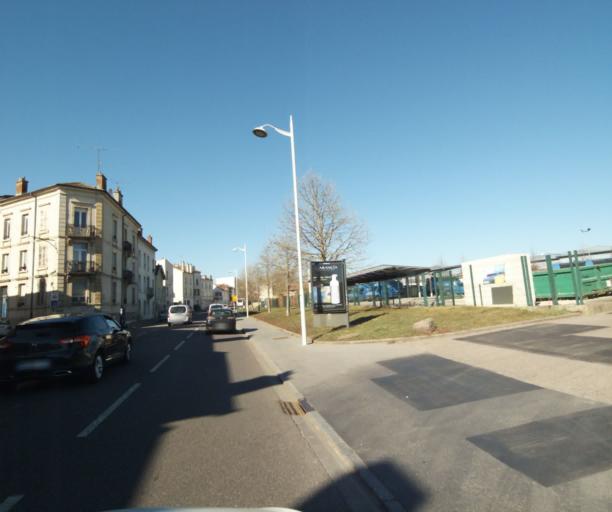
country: FR
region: Lorraine
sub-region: Departement de Meurthe-et-Moselle
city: Malzeville
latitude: 48.7012
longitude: 6.1845
